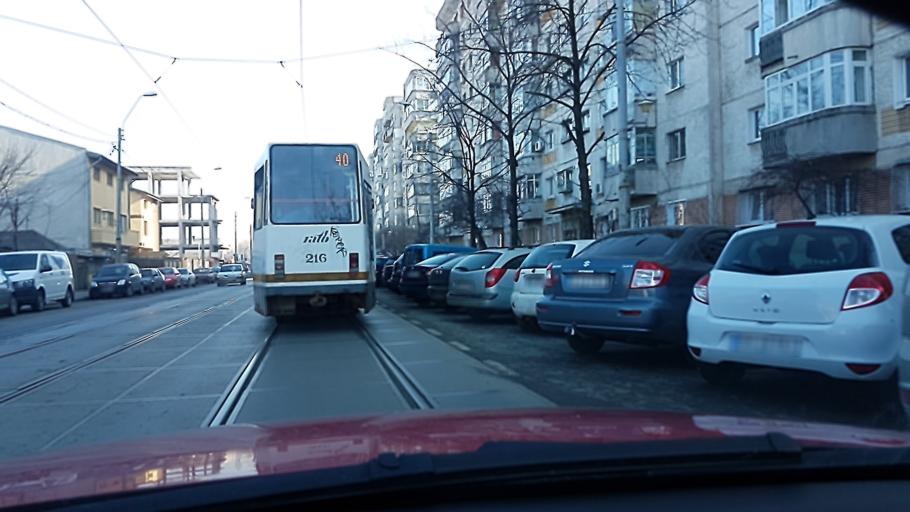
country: RO
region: Ilfov
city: Dobroesti
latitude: 44.4285
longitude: 26.1761
